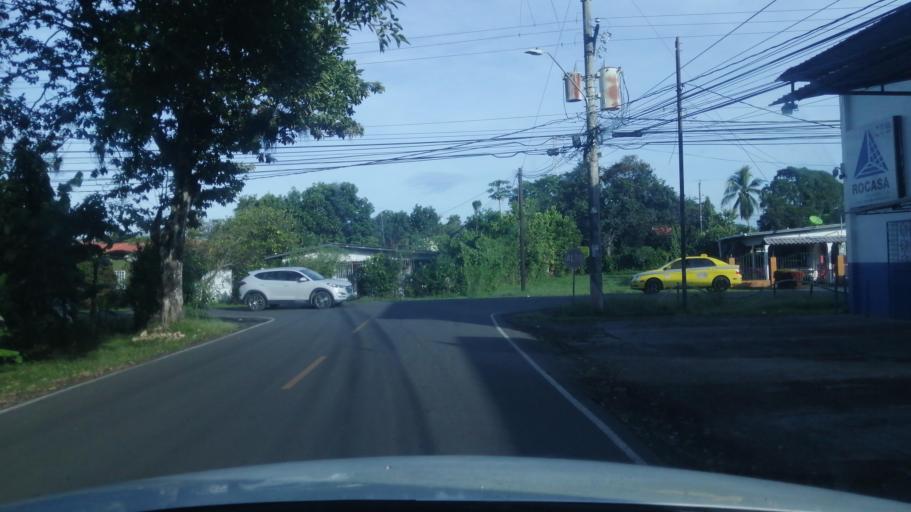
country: PA
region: Chiriqui
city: David
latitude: 8.4267
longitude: -82.4417
